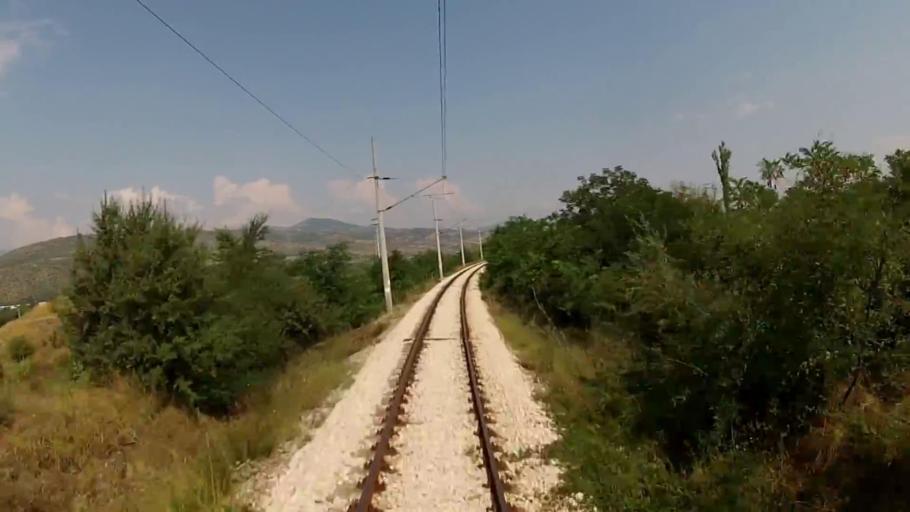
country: BG
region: Blagoevgrad
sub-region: Obshtina Sandanski
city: Sandanski
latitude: 41.5301
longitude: 23.2588
